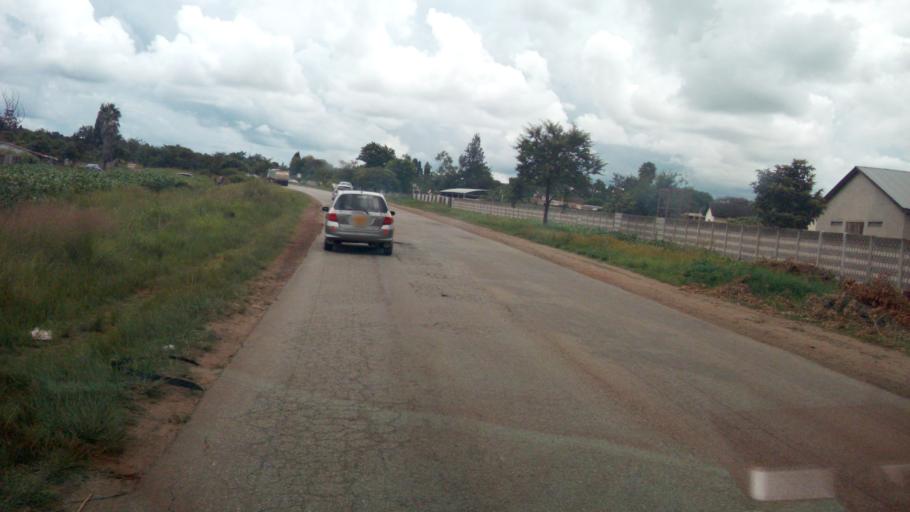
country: ZW
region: Harare
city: Harare
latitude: -17.7789
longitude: 30.9953
